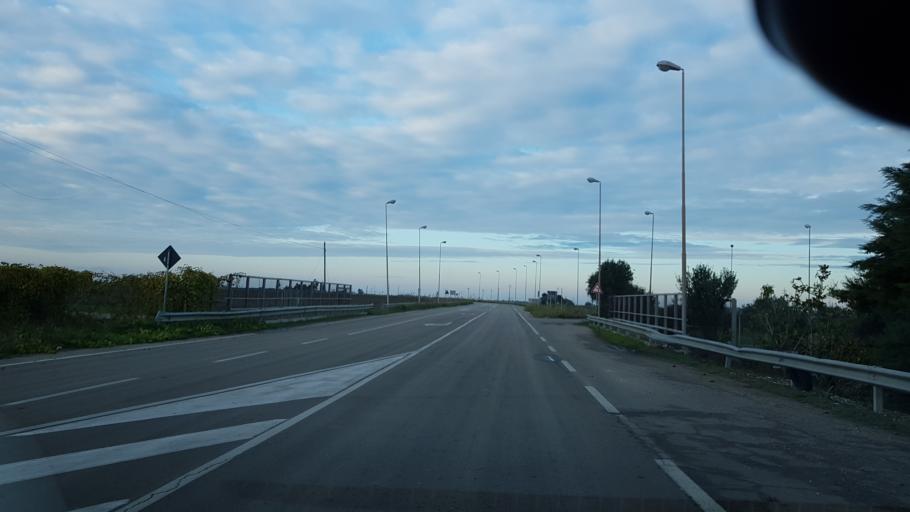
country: IT
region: Apulia
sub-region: Provincia di Brindisi
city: Tuturano
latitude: 40.5683
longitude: 18.0160
